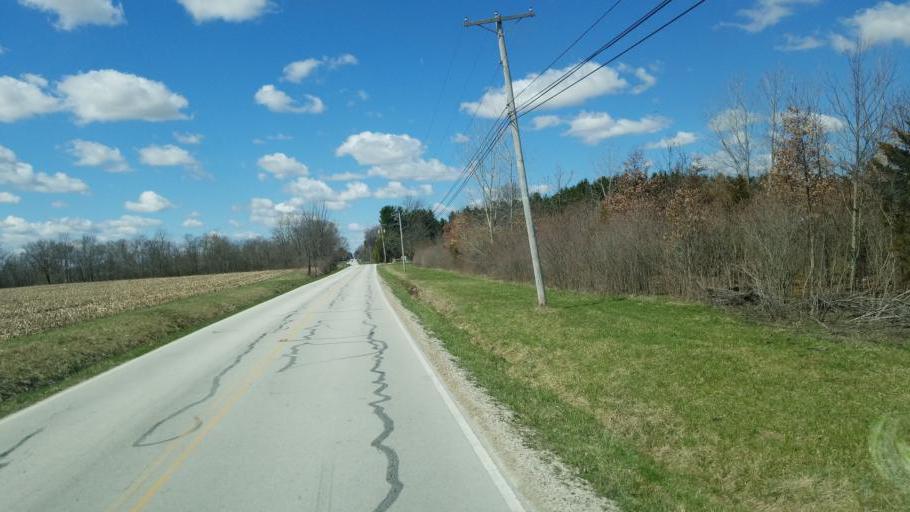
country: US
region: Ohio
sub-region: Sandusky County
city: Green Springs
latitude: 41.2569
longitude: -83.0730
